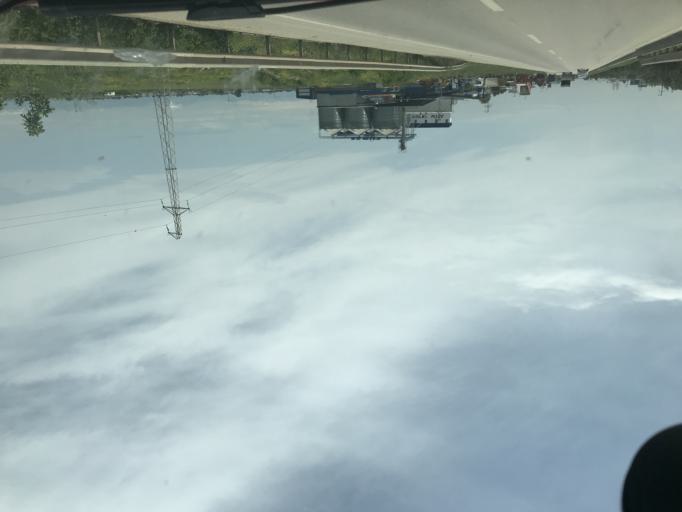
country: TR
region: Adana
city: Yuregir
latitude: 36.9778
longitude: 35.4701
